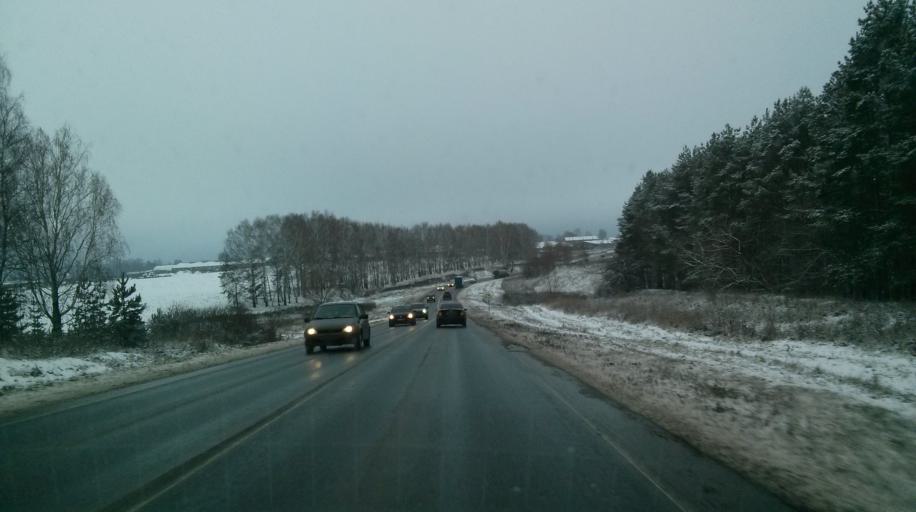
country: RU
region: Nizjnij Novgorod
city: Vorsma
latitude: 56.0432
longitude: 43.3861
